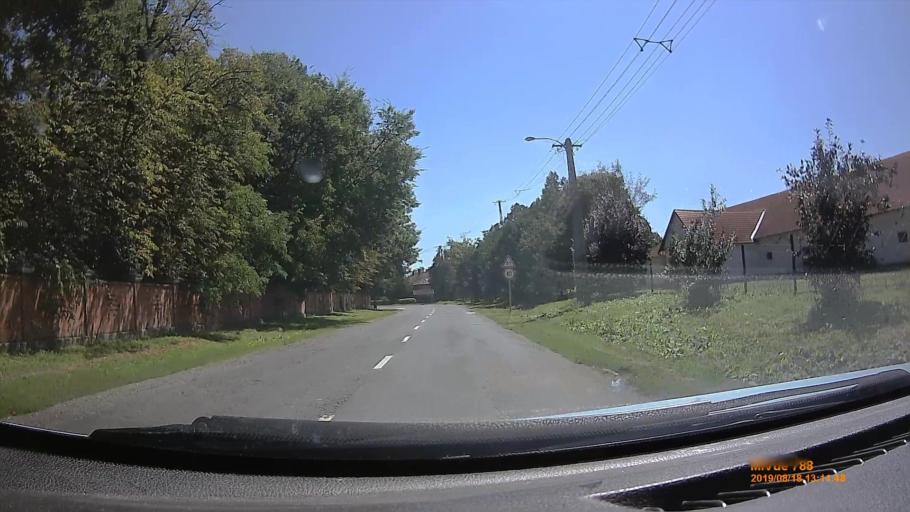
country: HU
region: Fejer
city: Sarbogard
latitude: 46.8727
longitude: 18.5413
